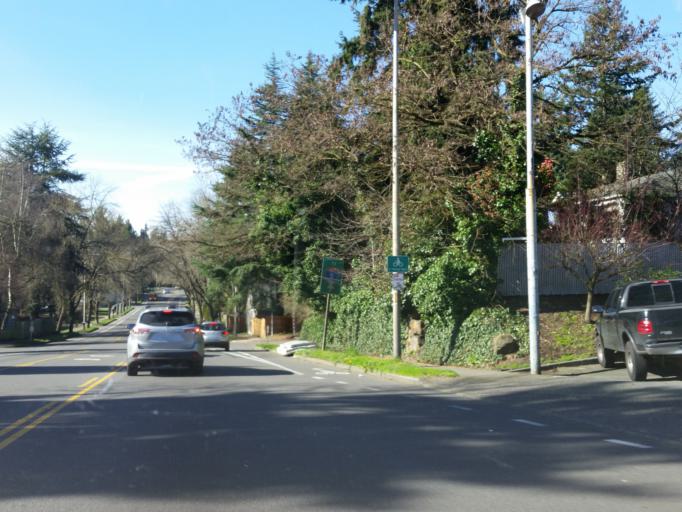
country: US
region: Washington
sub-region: King County
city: Shoreline
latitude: 47.7195
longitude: -122.3133
